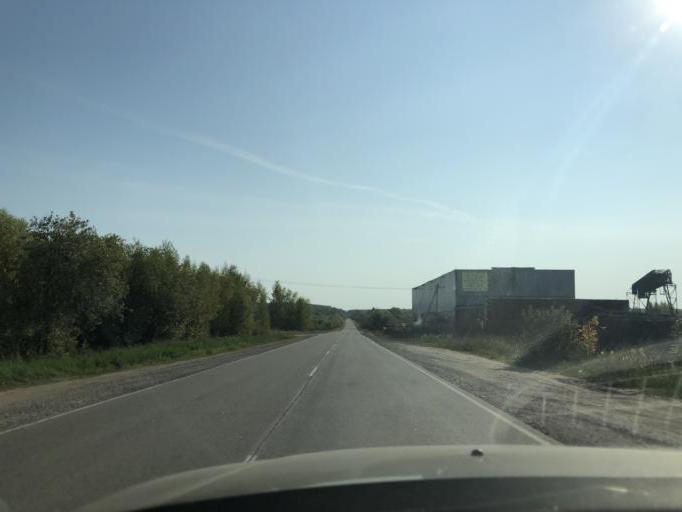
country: RU
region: Tula
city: Novogurovskiy
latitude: 54.4487
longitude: 37.3862
